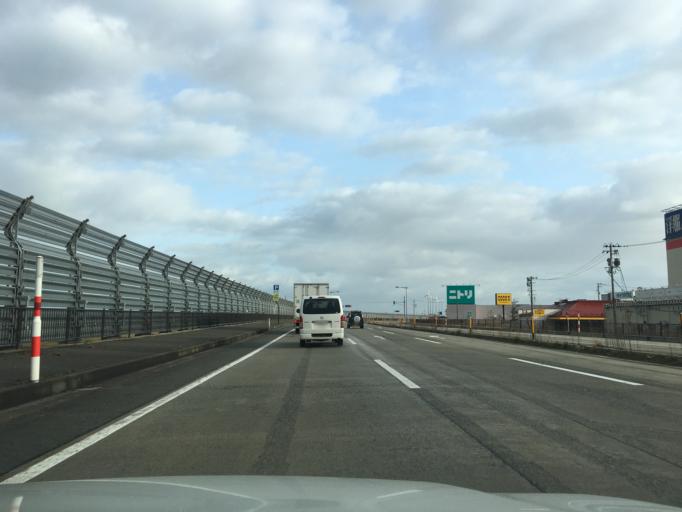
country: JP
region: Yamagata
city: Tsuruoka
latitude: 38.8169
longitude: 139.8328
